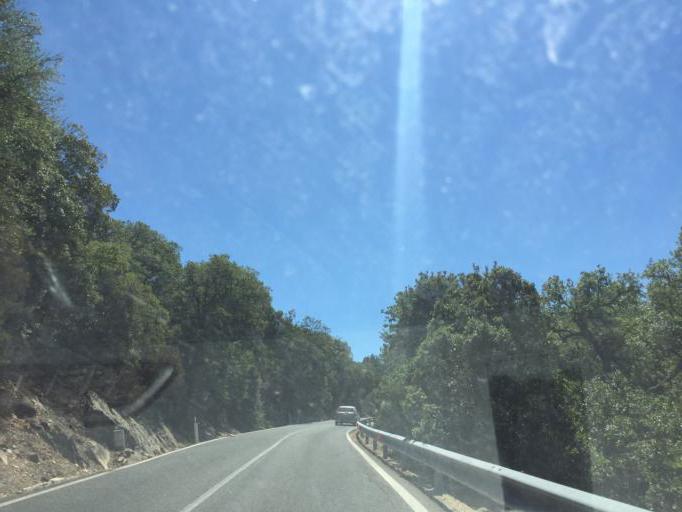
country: IT
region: Sardinia
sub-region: Provincia di Olbia-Tempio
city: Calangianus
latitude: 40.8986
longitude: 9.2257
